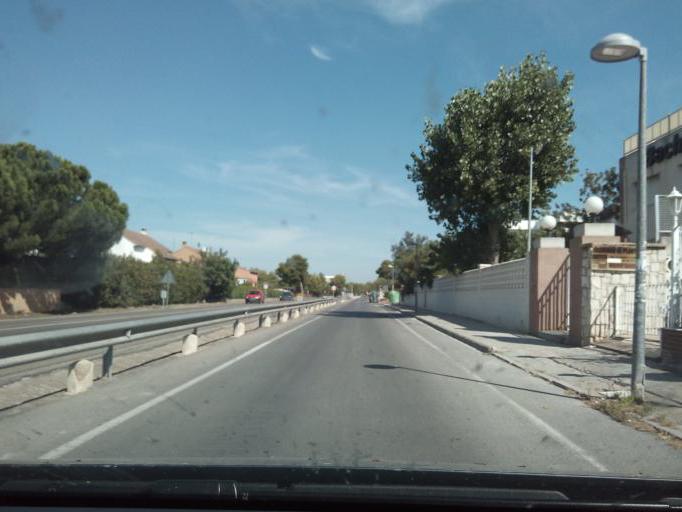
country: ES
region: Valencia
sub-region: Provincia de Valencia
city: Manises
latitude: 39.5326
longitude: -0.4737
